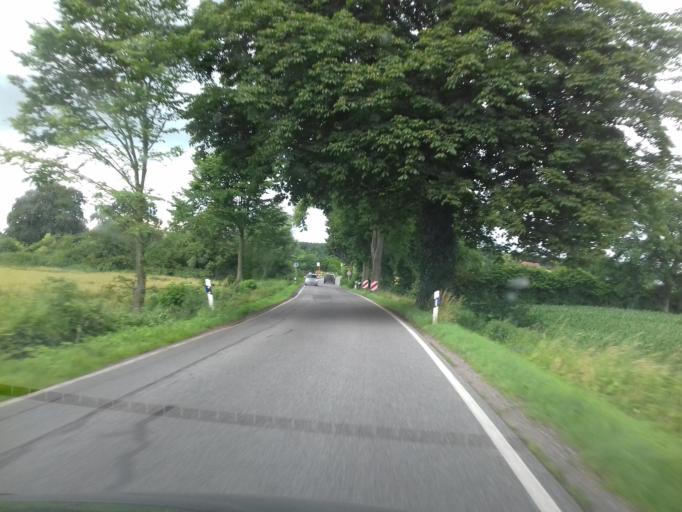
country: DE
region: Schleswig-Holstein
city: Elmenhorst
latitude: 53.7729
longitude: 10.2526
